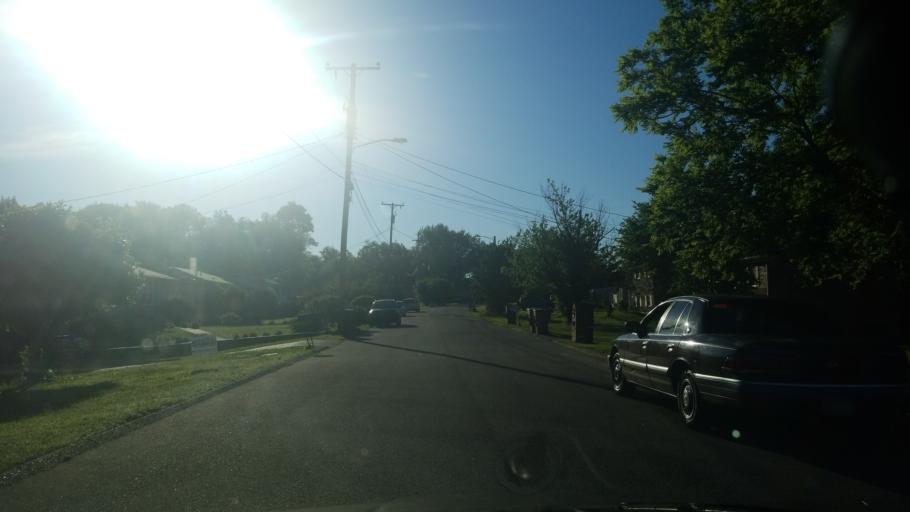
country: US
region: Tennessee
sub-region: Davidson County
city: Nashville
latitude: 36.2413
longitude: -86.7719
